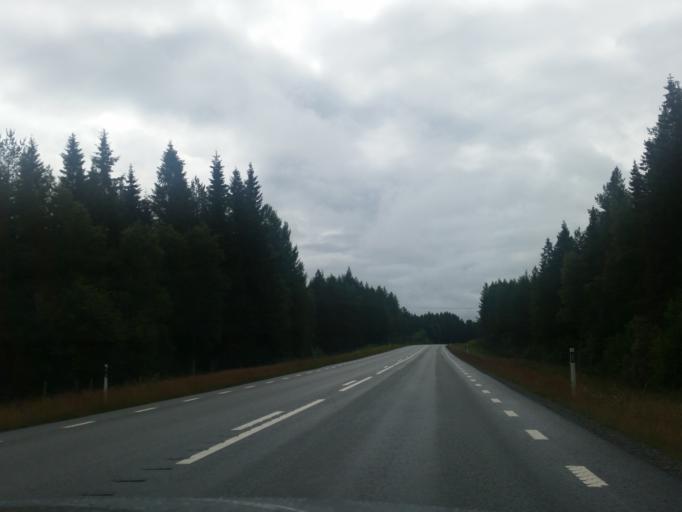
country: SE
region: Vaesterbotten
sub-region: Robertsfors Kommun
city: Robertsfors
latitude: 64.0277
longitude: 20.8413
